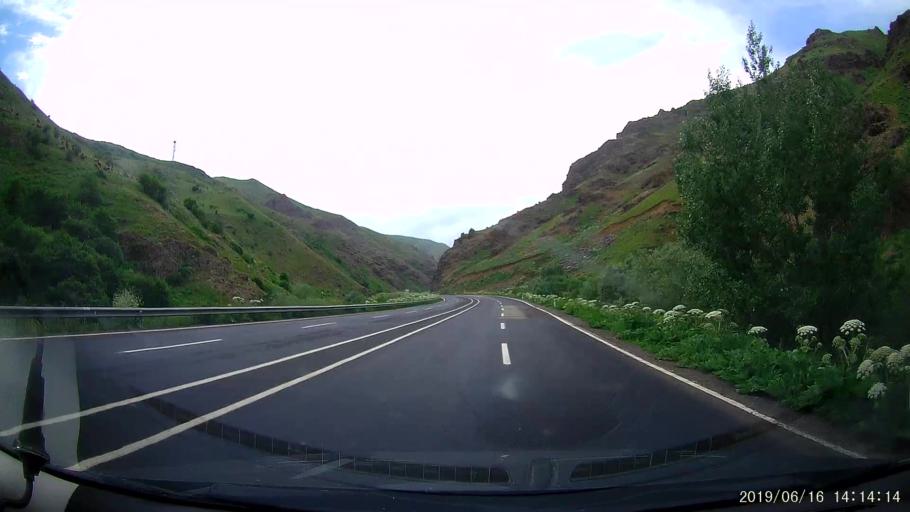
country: TR
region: Agri
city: Tahir
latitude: 39.7948
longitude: 42.5018
